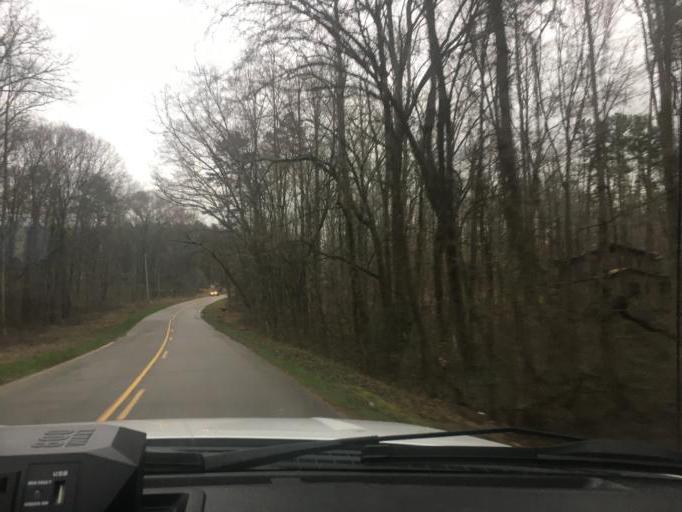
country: US
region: Georgia
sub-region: Dawson County
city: Dawsonville
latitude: 34.4435
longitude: -84.1930
